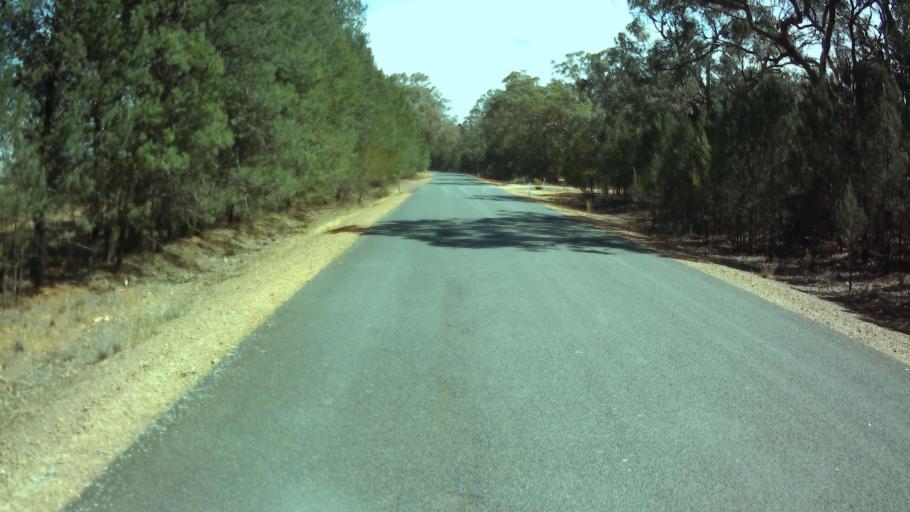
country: AU
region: New South Wales
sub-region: Weddin
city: Grenfell
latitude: -34.0113
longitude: 148.1296
